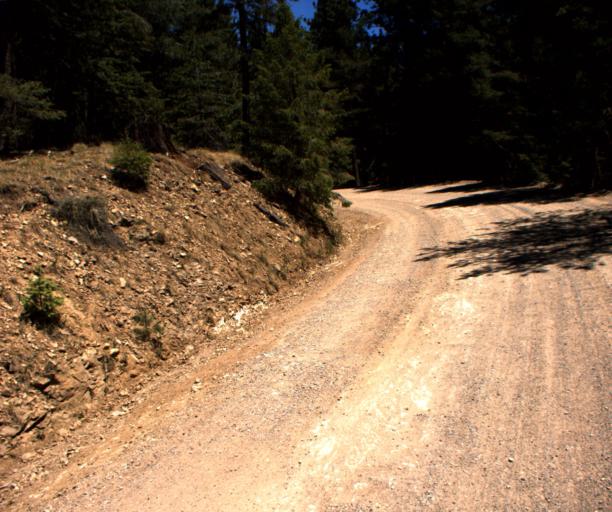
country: US
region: Arizona
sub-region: Graham County
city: Swift Trail Junction
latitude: 32.6725
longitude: -109.8863
